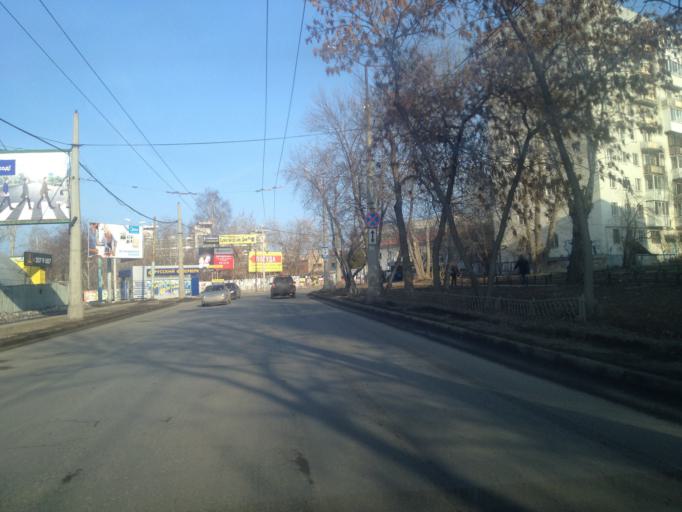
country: RU
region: Sverdlovsk
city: Yekaterinburg
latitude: 56.8238
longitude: 60.5682
